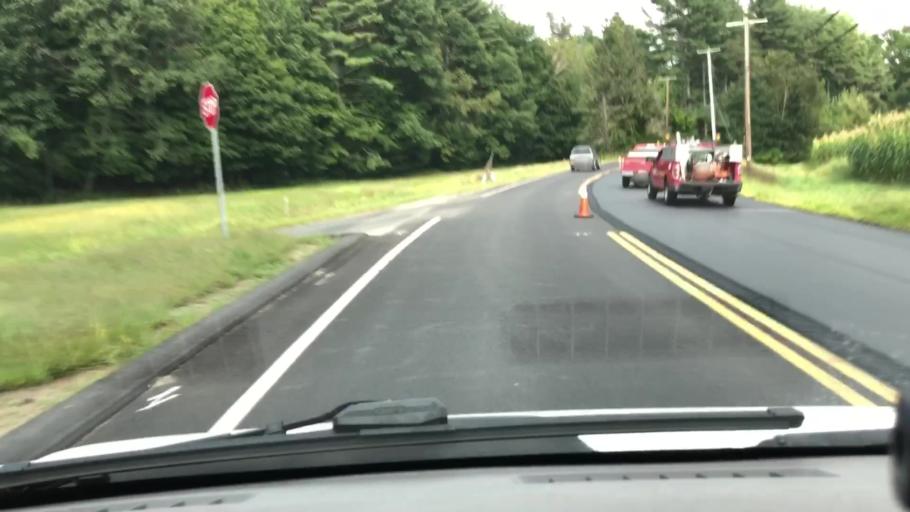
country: US
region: Massachusetts
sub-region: Franklin County
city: Buckland
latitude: 42.6238
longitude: -72.7848
